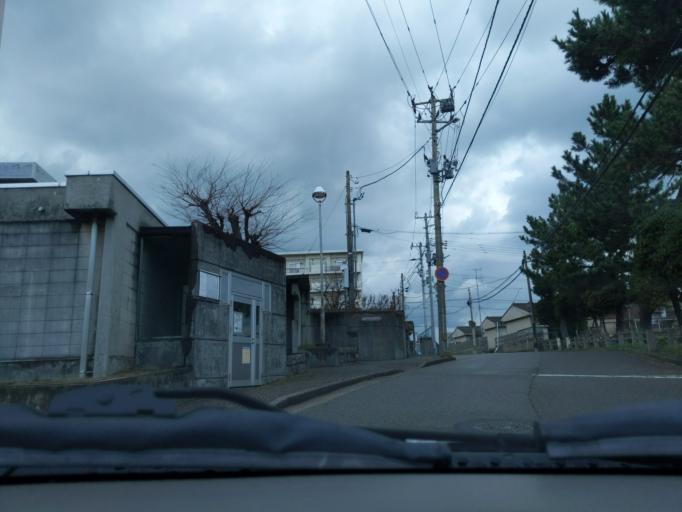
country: JP
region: Niigata
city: Niigata-shi
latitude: 37.9323
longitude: 139.0431
